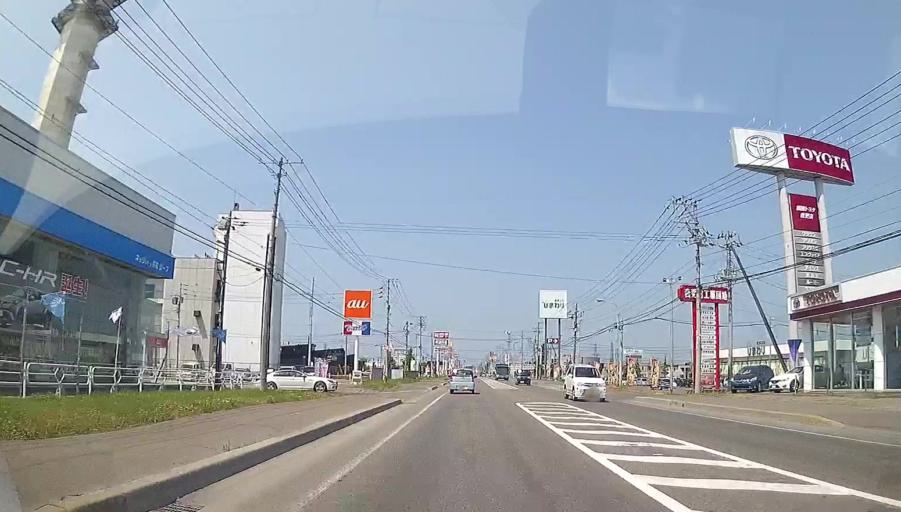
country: JP
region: Hokkaido
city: Otofuke
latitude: 42.9603
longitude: 143.2063
